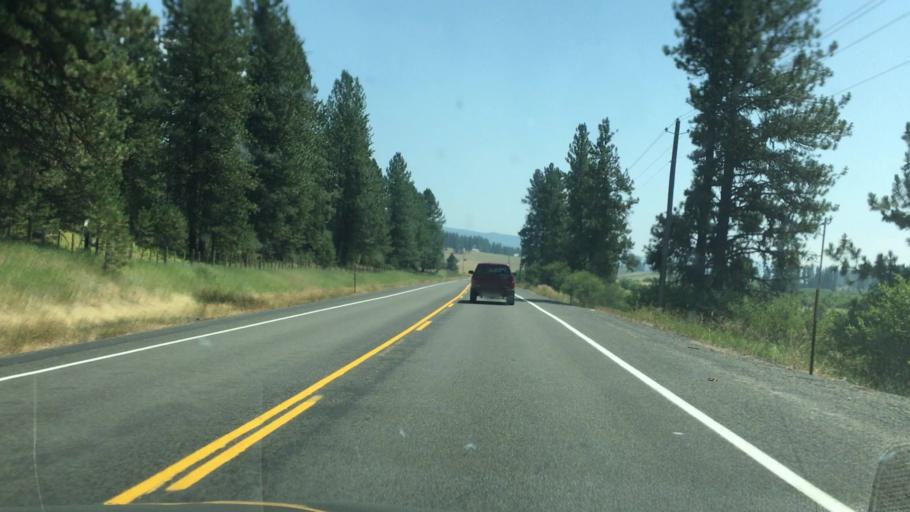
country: US
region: Idaho
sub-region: Valley County
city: McCall
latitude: 45.0791
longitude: -116.3020
